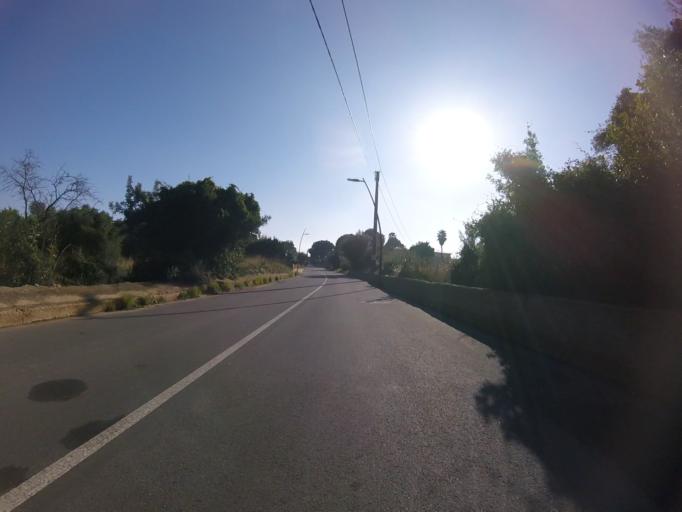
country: ES
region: Valencia
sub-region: Provincia de Castello
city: Peniscola
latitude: 40.3837
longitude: 0.3810
